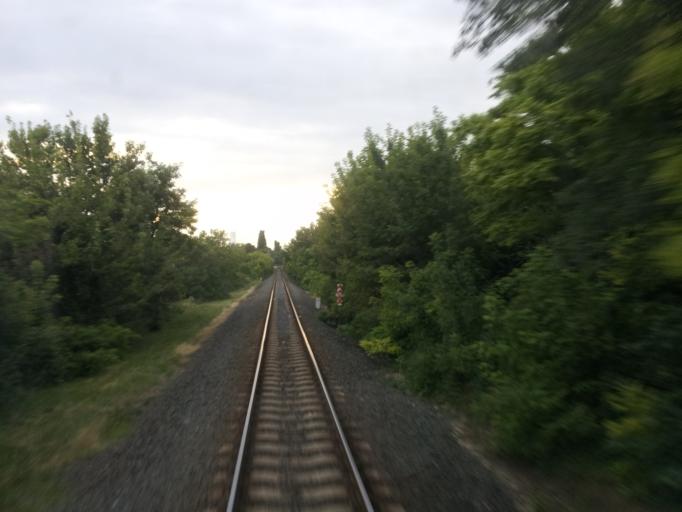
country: HU
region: Veszprem
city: Balatonkenese
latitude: 47.0229
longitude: 18.1418
